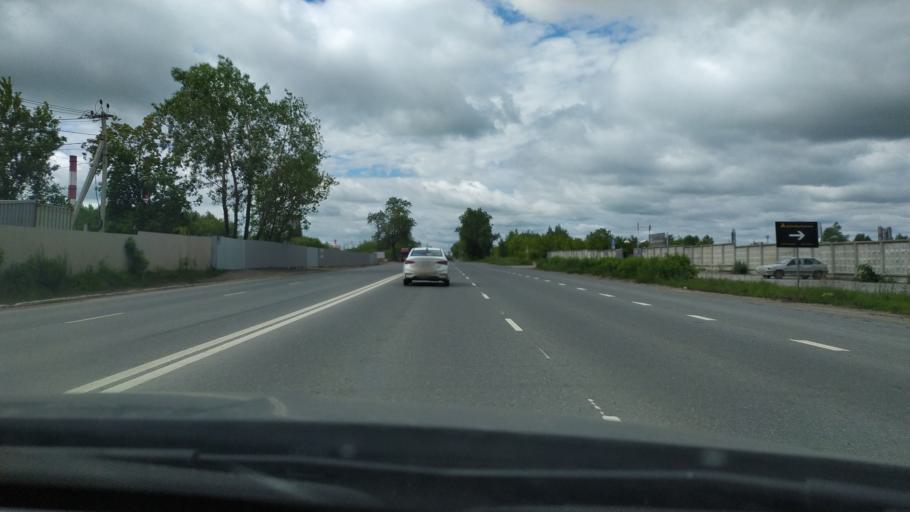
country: RU
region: Perm
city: Kondratovo
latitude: 57.9328
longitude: 56.1511
